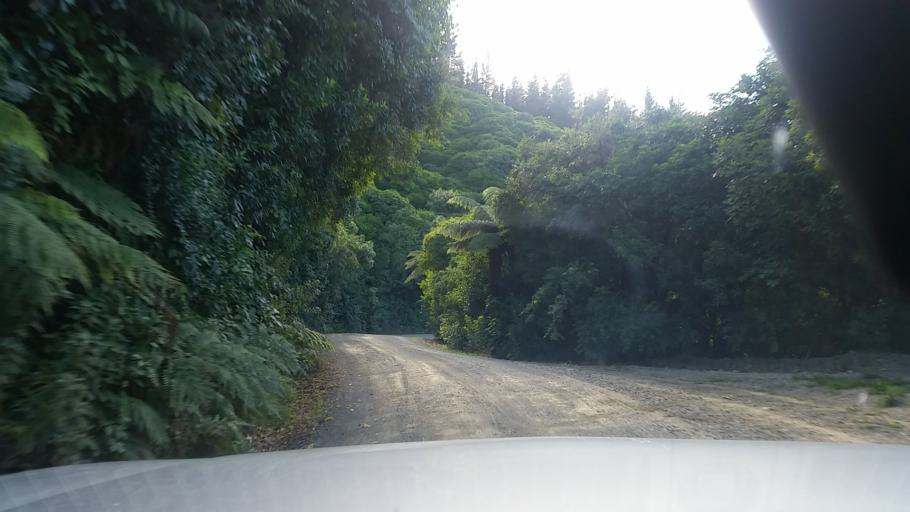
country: NZ
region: Marlborough
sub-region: Marlborough District
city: Picton
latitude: -41.2974
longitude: 174.1204
